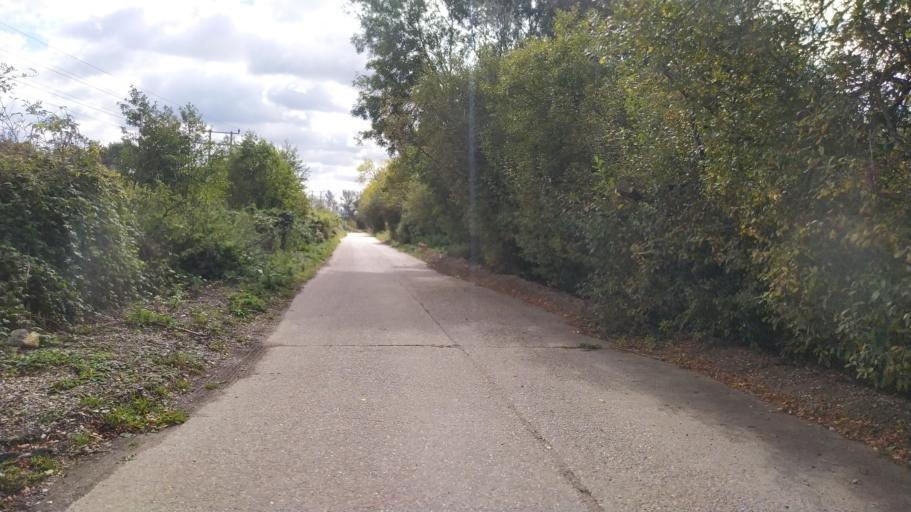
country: GB
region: England
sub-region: Reading
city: Reading
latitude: 51.4291
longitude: -1.0048
